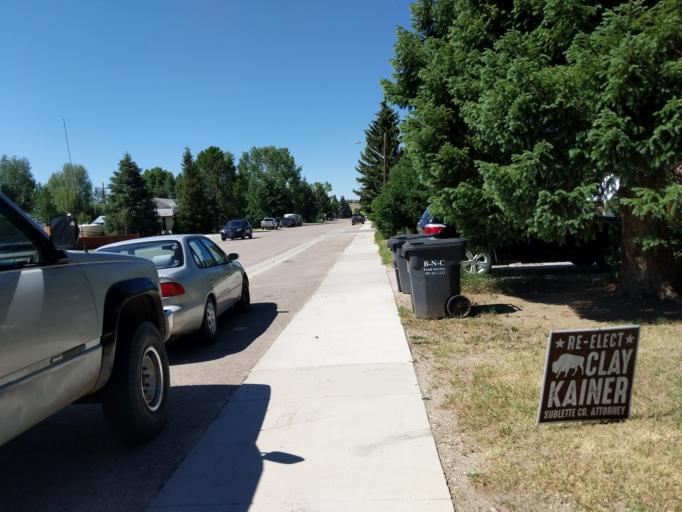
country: US
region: Wyoming
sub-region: Sublette County
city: Pinedale
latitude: 42.8683
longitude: -109.8612
